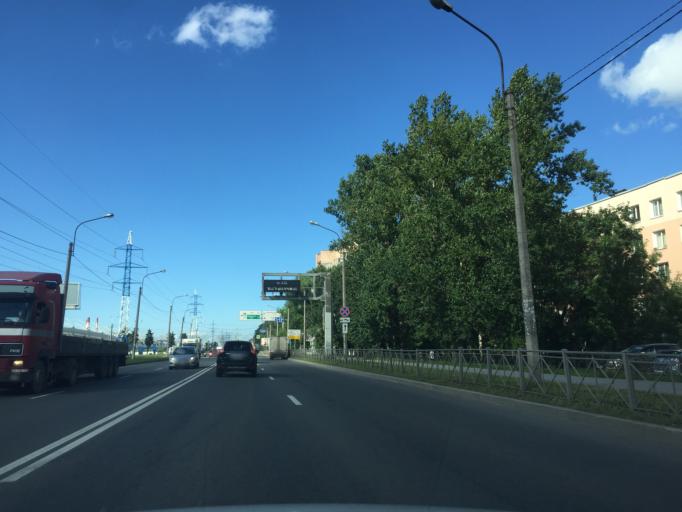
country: RU
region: St.-Petersburg
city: Avtovo
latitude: 59.8500
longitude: 30.2923
